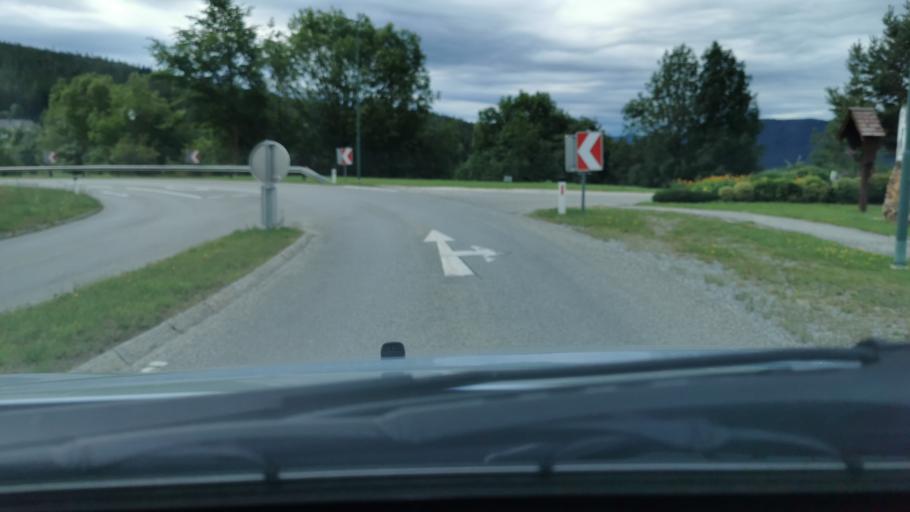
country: AT
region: Styria
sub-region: Politischer Bezirk Weiz
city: Fischbach
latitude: 47.4365
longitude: 15.6534
